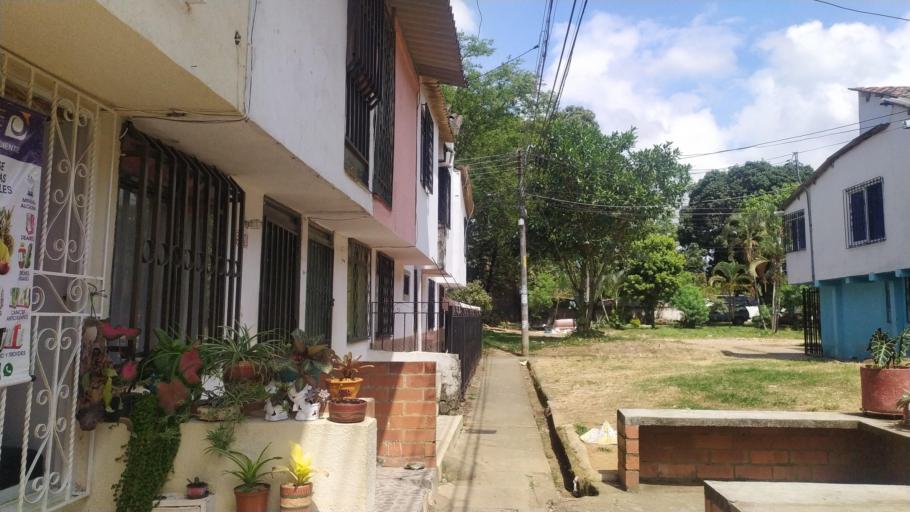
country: CO
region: Valle del Cauca
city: Jamundi
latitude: 3.2528
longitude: -76.5426
